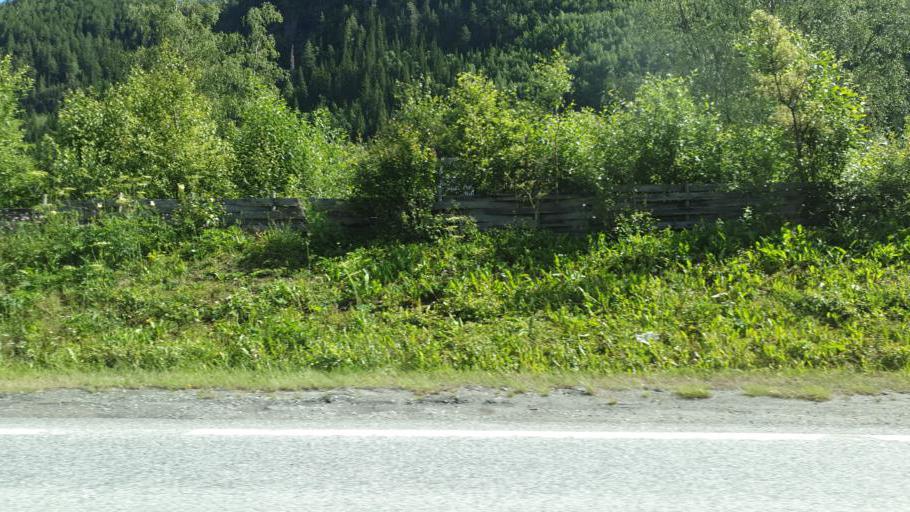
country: NO
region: Sor-Trondelag
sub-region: Midtre Gauldal
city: Storen
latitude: 63.0003
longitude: 10.2383
